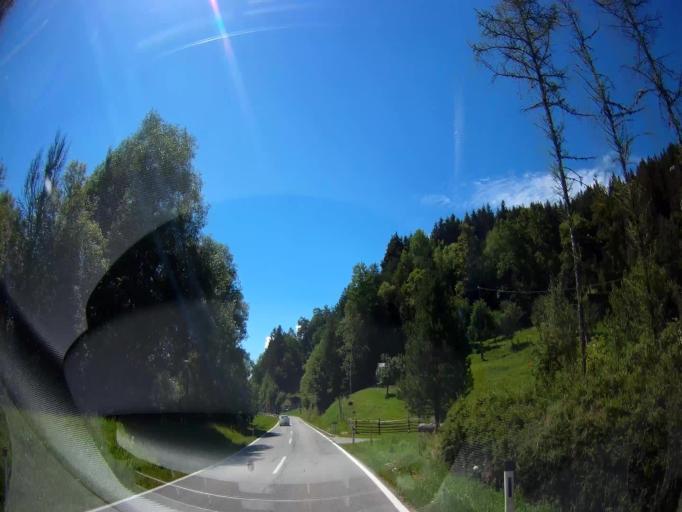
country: AT
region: Carinthia
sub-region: Politischer Bezirk Sankt Veit an der Glan
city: Glodnitz
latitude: 46.8501
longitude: 14.1979
